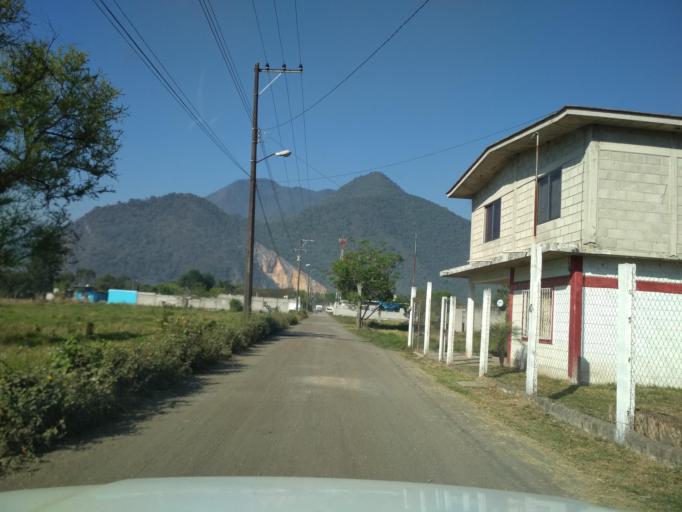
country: MX
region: Veracruz
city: Jalapilla
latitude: 18.8247
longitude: -97.0798
